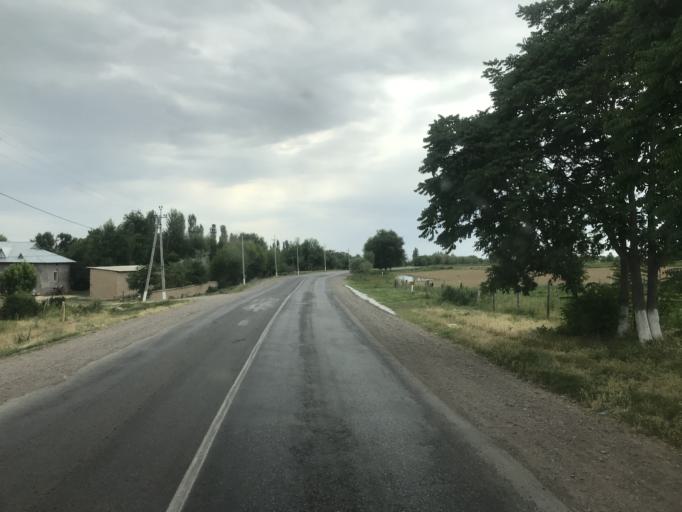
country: KZ
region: Ongtustik Qazaqstan
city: Saryaghash
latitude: 41.3775
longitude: 69.0143
